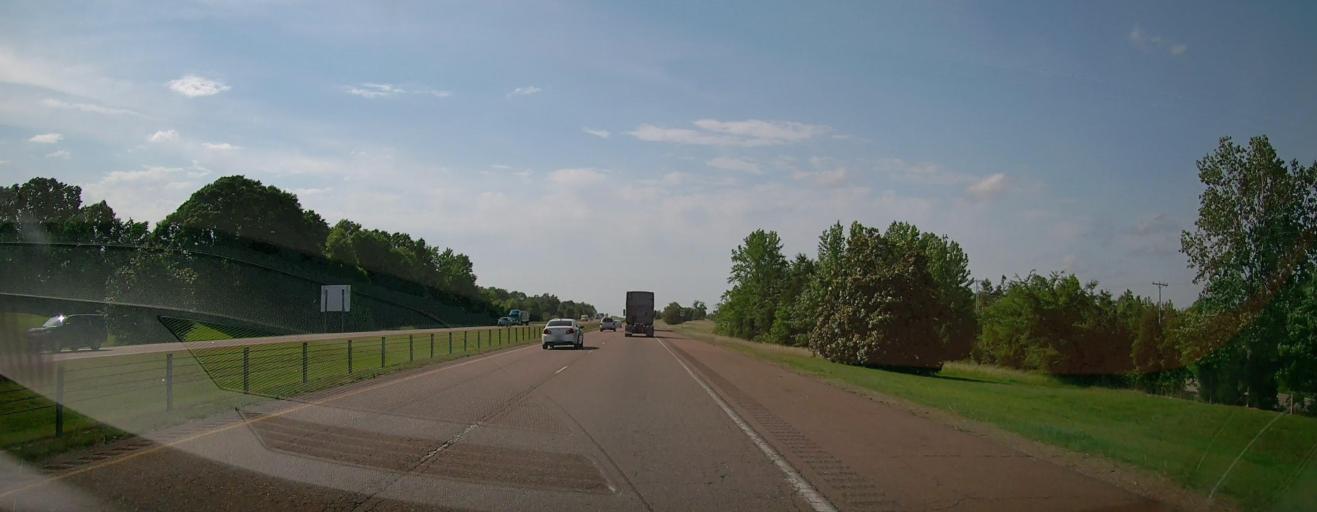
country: US
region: Mississippi
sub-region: De Soto County
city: Olive Branch
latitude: 34.9662
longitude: -89.8558
